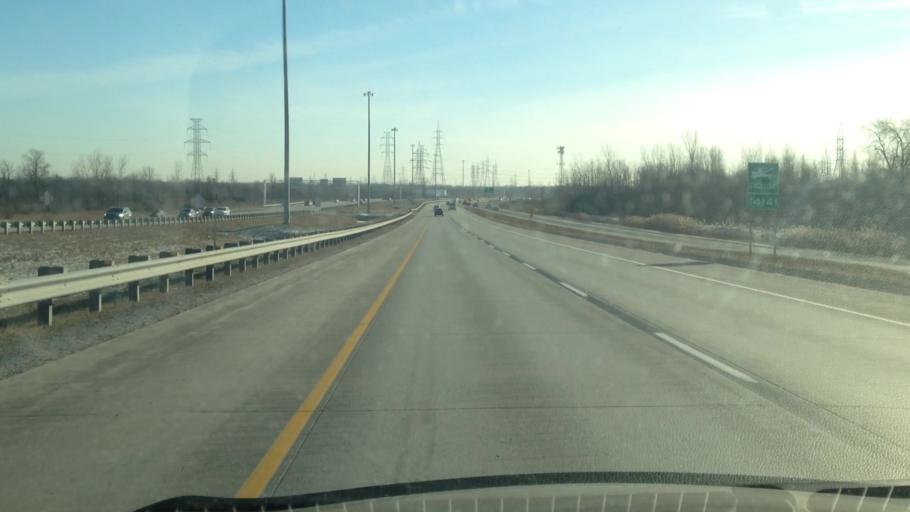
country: CA
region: Quebec
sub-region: Laurentides
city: Boisbriand
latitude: 45.5977
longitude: -73.8599
